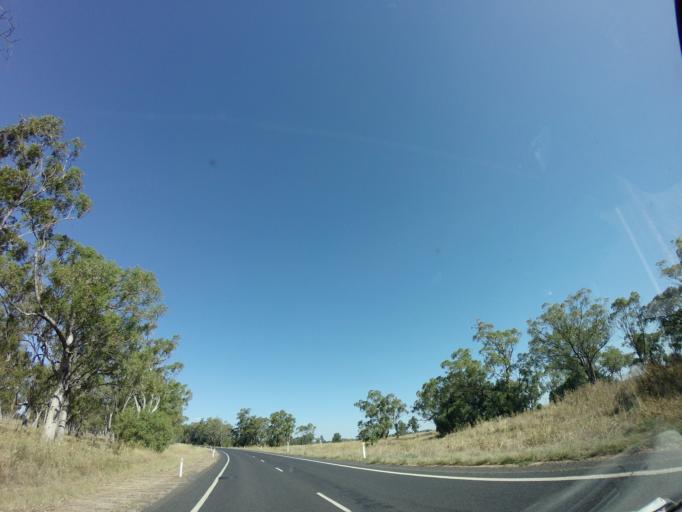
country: AU
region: New South Wales
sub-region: Narromine
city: Narromine
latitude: -31.6464
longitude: 147.9165
